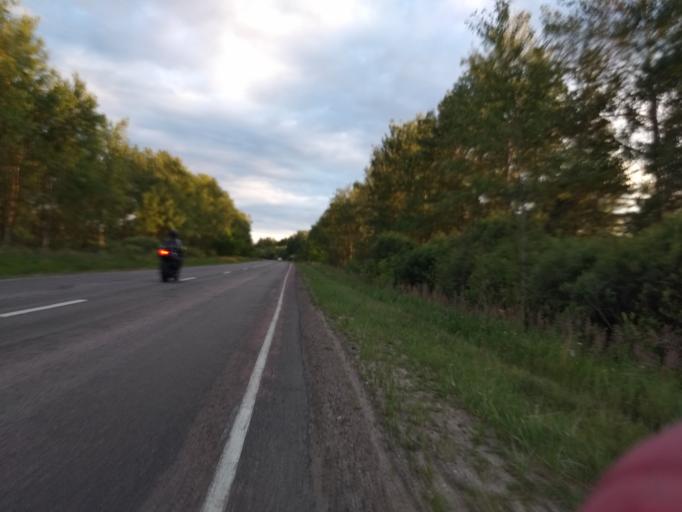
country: RU
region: Moskovskaya
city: Misheronskiy
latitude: 55.6067
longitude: 39.7112
